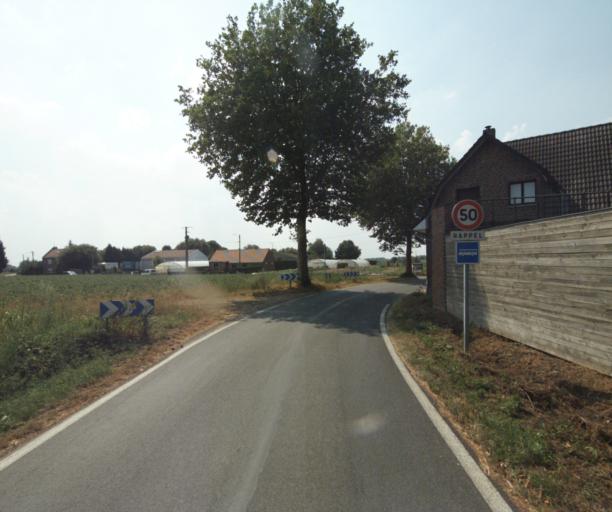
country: FR
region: Nord-Pas-de-Calais
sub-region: Departement du Nord
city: Linselles
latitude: 50.7242
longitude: 3.0415
